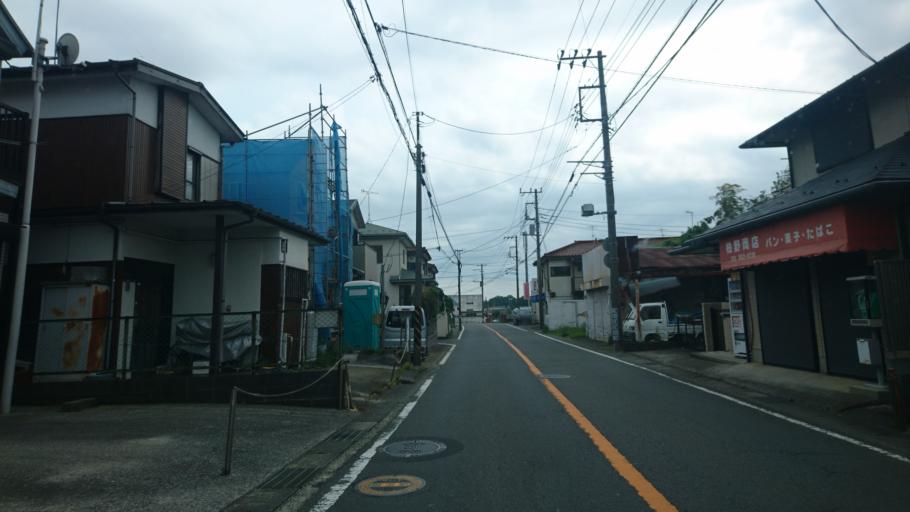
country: JP
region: Kanagawa
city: Fujisawa
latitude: 35.4149
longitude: 139.4795
